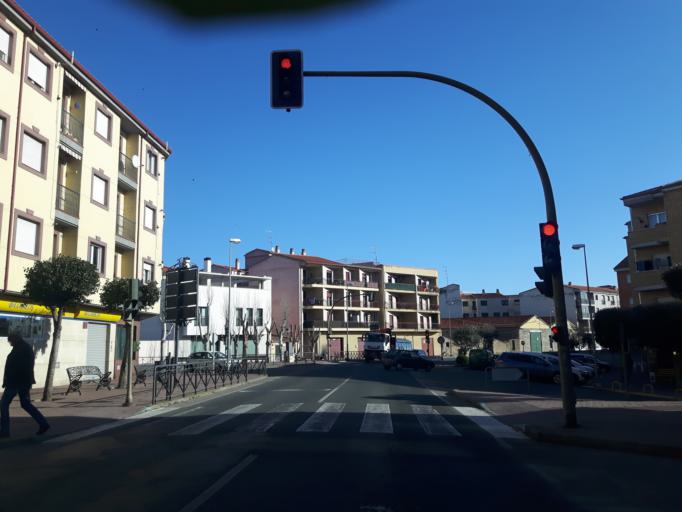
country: ES
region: Castille and Leon
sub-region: Provincia de Salamanca
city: Alba de Tormes
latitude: 40.8258
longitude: -5.5091
